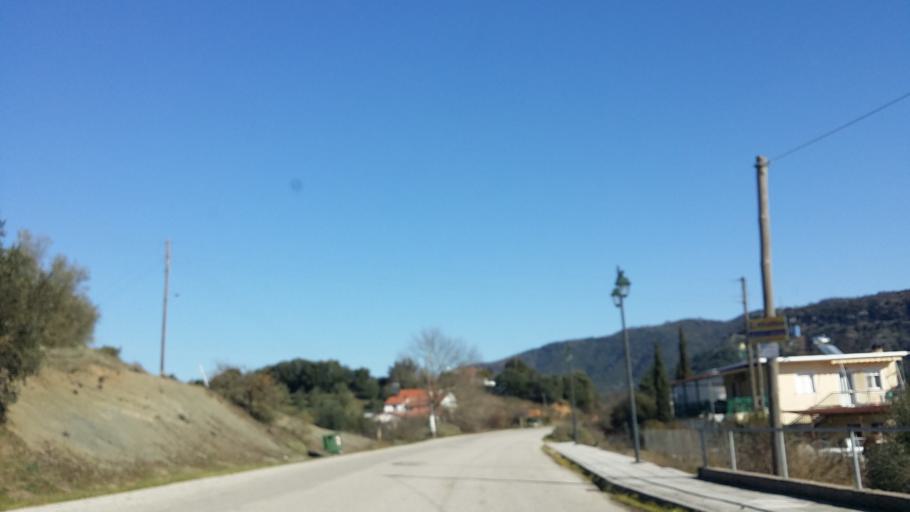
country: GR
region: West Greece
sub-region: Nomos Aitolias kai Akarnanias
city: Sardinia
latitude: 38.8575
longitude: 21.3366
